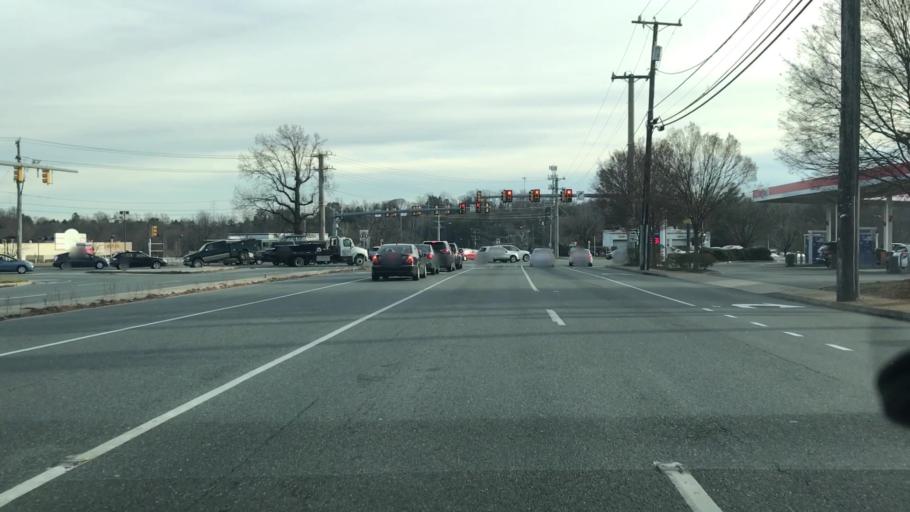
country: US
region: Virginia
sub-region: City of Charlottesville
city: Charlottesville
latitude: 38.0629
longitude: -78.4921
